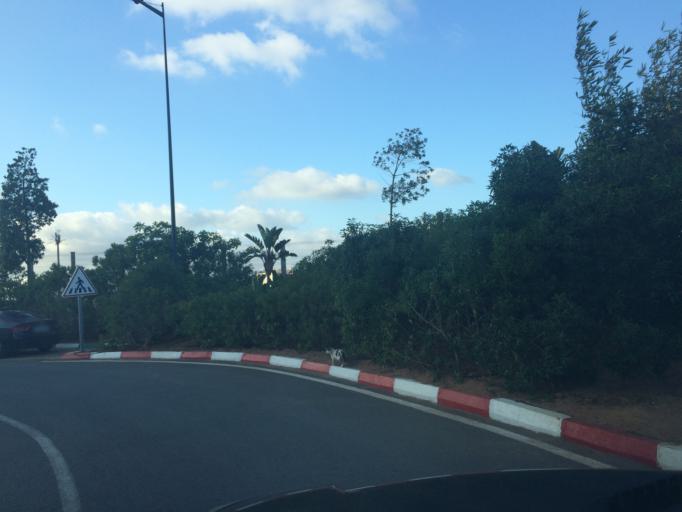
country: MA
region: Rabat-Sale-Zemmour-Zaer
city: Sale
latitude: 33.9857
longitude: -6.7204
